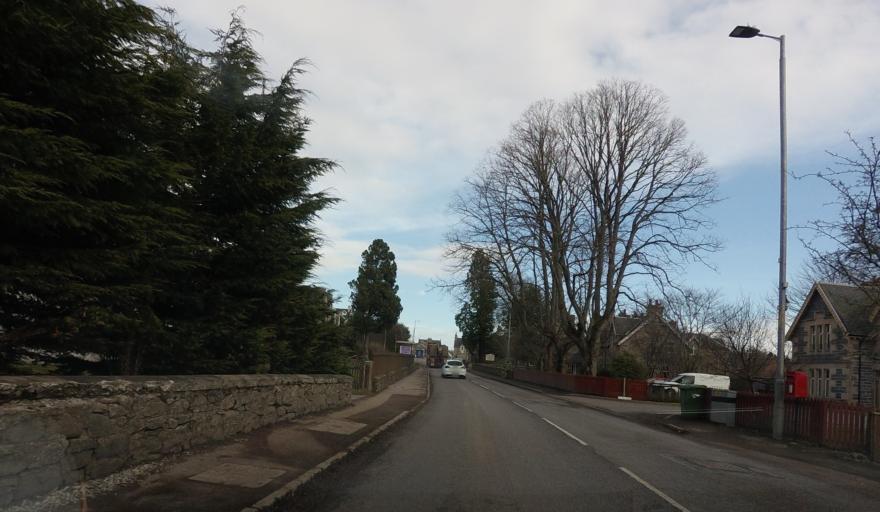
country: GB
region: Scotland
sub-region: Highland
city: Kingussie
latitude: 57.0789
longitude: -4.0562
